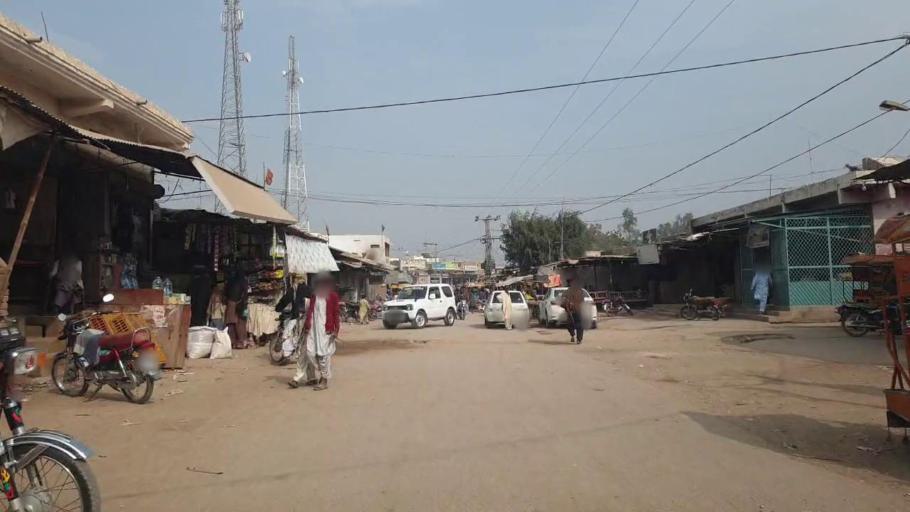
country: PK
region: Sindh
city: Sann
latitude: 26.0396
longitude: 68.1369
